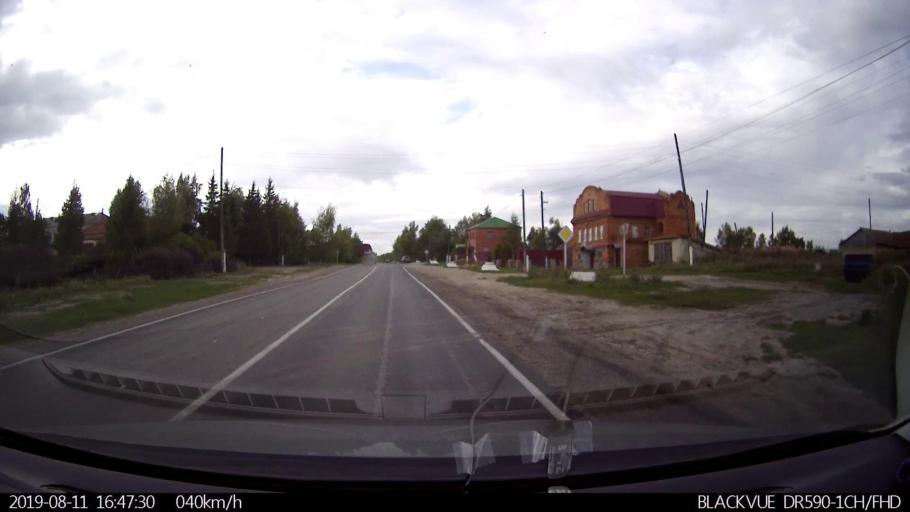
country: RU
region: Ulyanovsk
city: Mayna
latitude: 54.2023
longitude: 47.6963
